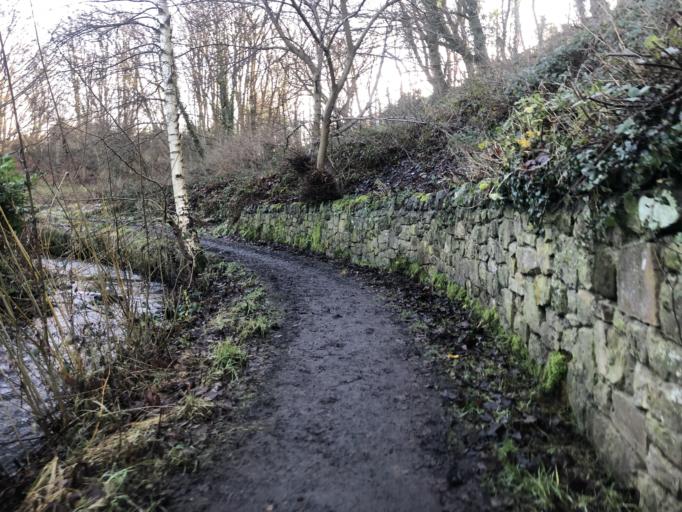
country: GB
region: Scotland
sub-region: Midlothian
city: Loanhead
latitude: 55.9096
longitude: -3.1477
